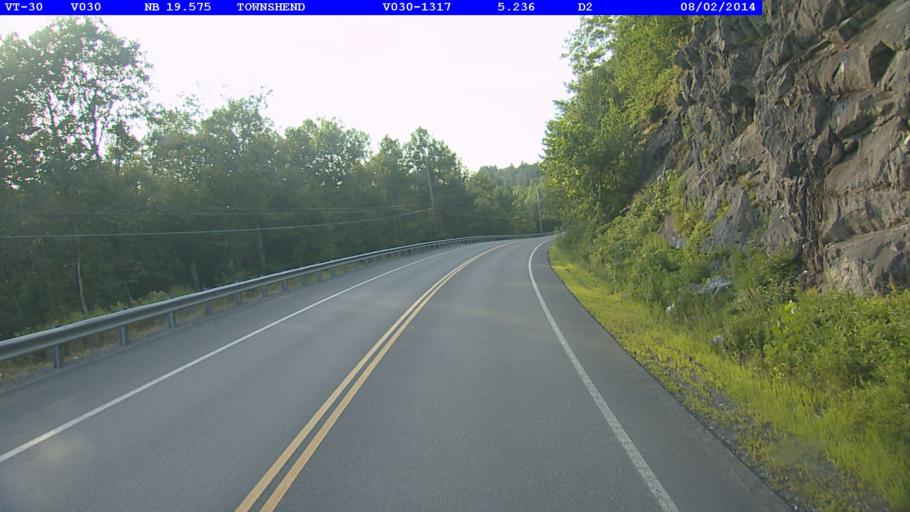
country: US
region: Vermont
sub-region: Windham County
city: Newfane
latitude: 43.0682
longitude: -72.7031
